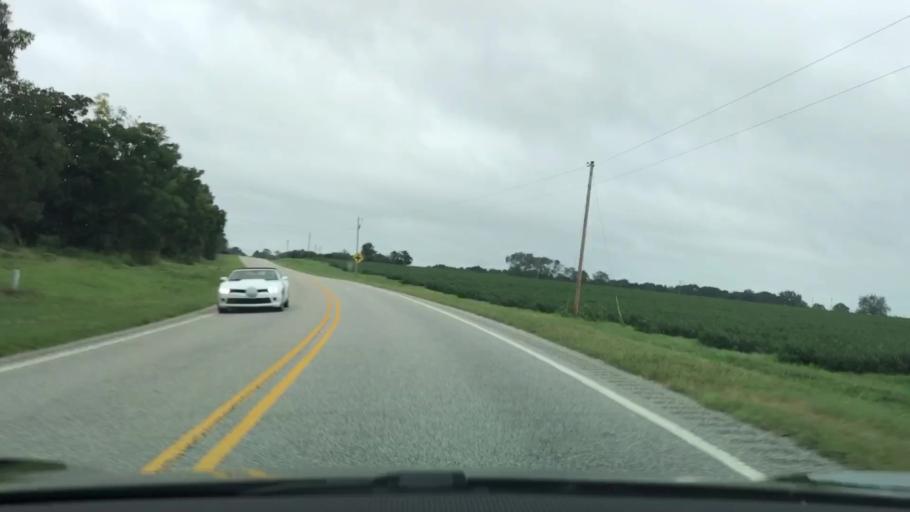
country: US
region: Alabama
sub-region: Coffee County
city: Elba
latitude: 31.3346
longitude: -86.1315
